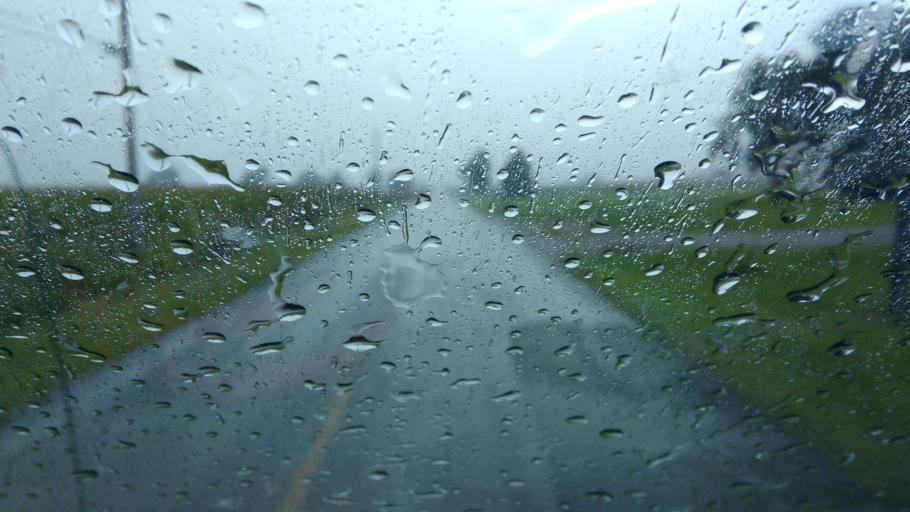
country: US
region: Ohio
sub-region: Hardin County
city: Kenton
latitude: 40.6865
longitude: -83.5379
